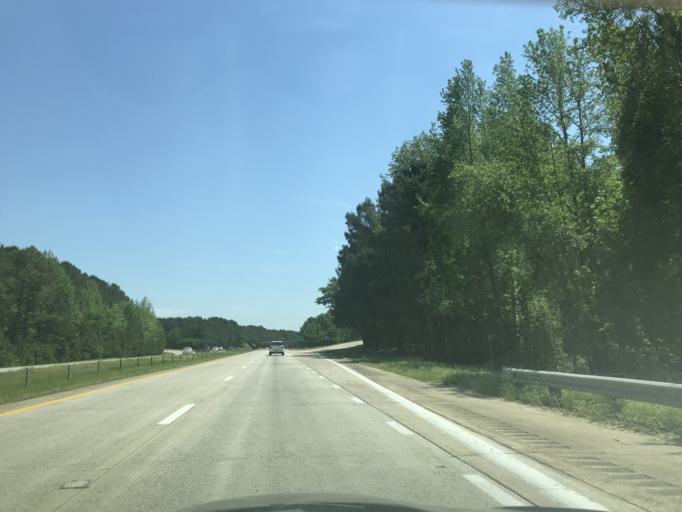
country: US
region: North Carolina
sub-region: Johnston County
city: Benson
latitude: 35.5201
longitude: -78.5603
